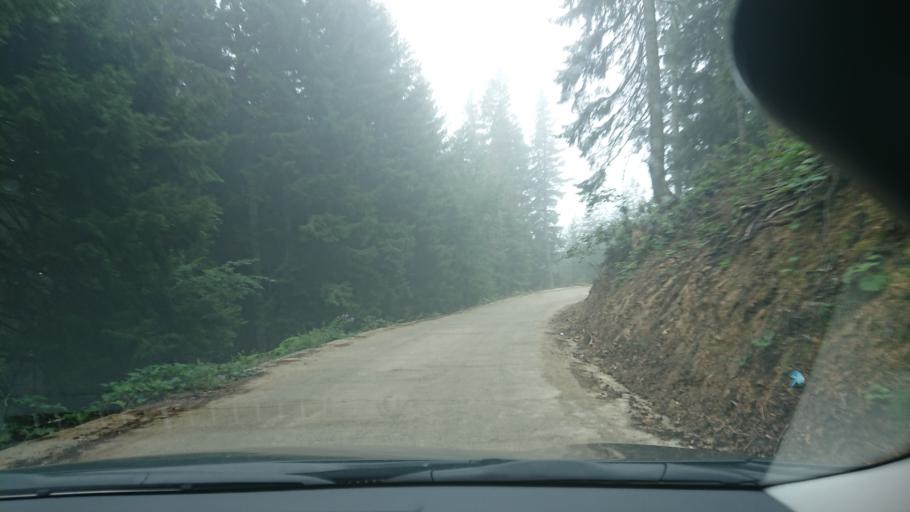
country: TR
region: Gumushane
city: Kurtun
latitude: 40.6646
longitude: 39.0168
